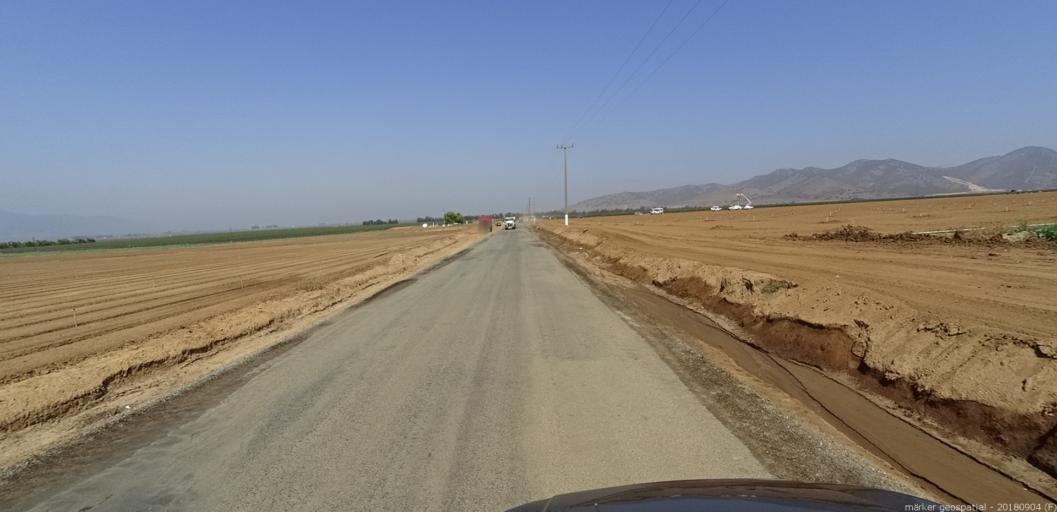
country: US
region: California
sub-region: Monterey County
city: Gonzales
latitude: 36.5414
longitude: -121.4281
